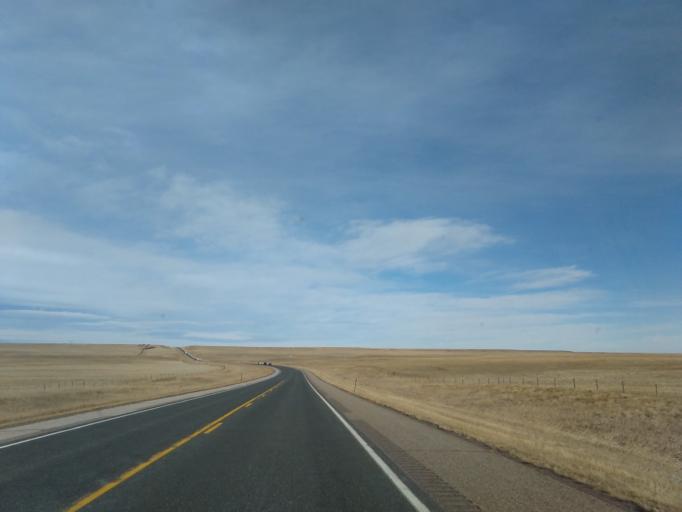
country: US
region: Wyoming
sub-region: Laramie County
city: Pine Bluffs
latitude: 41.5740
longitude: -104.2756
